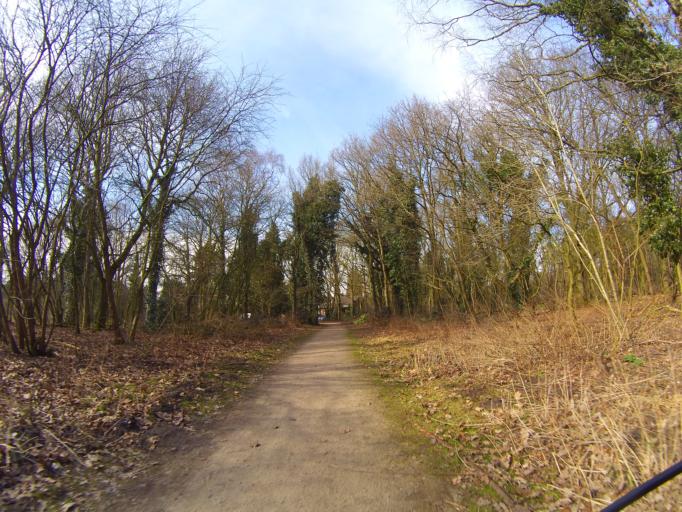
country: NL
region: North Holland
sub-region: Gemeente Hilversum
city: Hilversum
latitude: 52.2361
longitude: 5.2005
